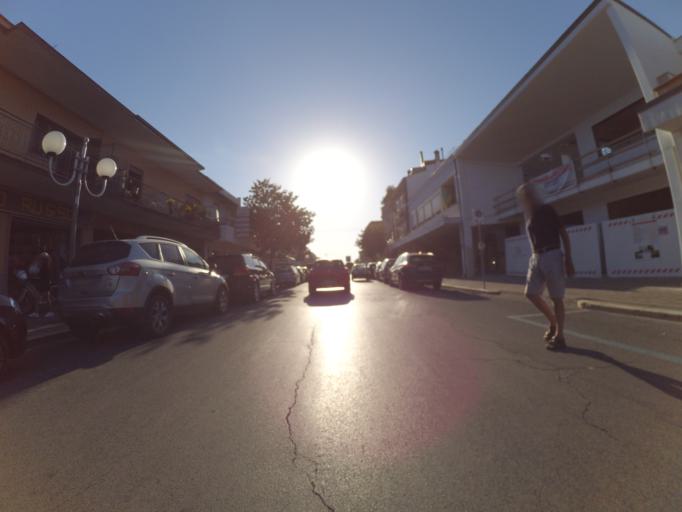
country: IT
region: Latium
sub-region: Provincia di Latina
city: San Felice Circeo
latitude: 41.2427
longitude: 13.0941
